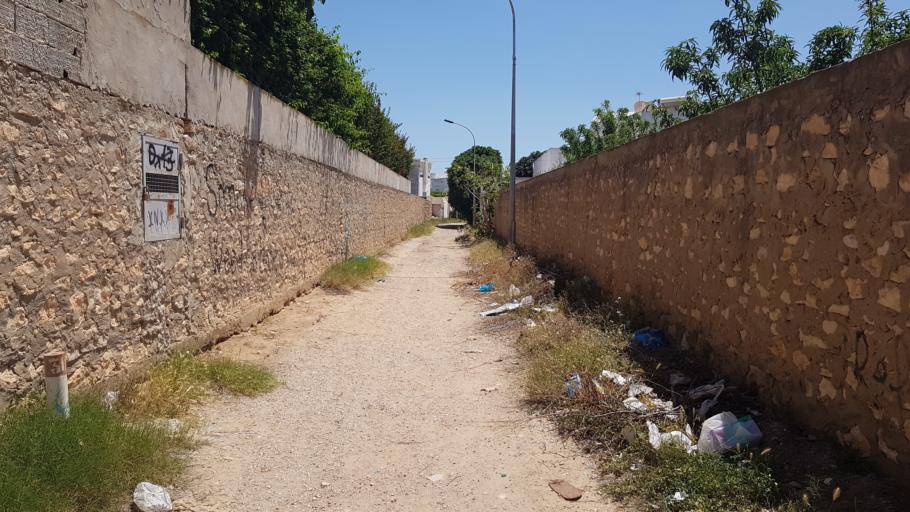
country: TN
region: Safaqis
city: Al Qarmadah
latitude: 34.8264
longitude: 10.7611
